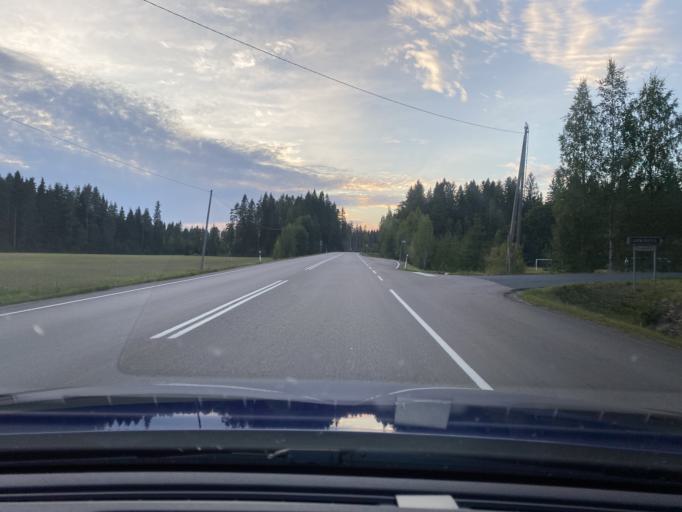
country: FI
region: Satakunta
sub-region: Pohjois-Satakunta
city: Kankaanpaeae
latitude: 61.8575
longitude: 22.3236
